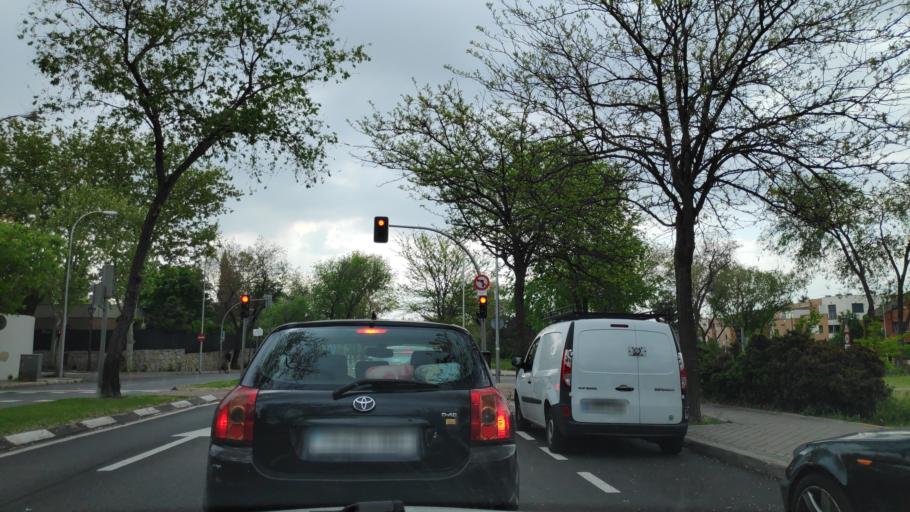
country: ES
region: Madrid
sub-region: Provincia de Madrid
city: Pozuelo de Alarcon
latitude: 40.4611
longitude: -3.7911
